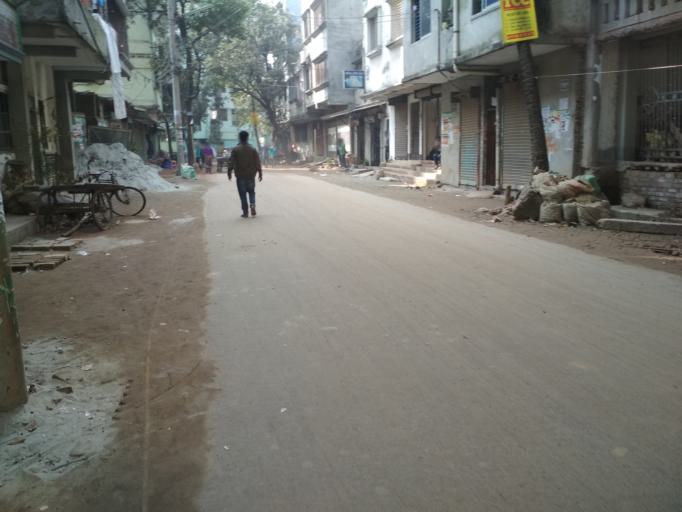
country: BD
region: Dhaka
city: Azimpur
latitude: 23.8098
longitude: 90.3727
